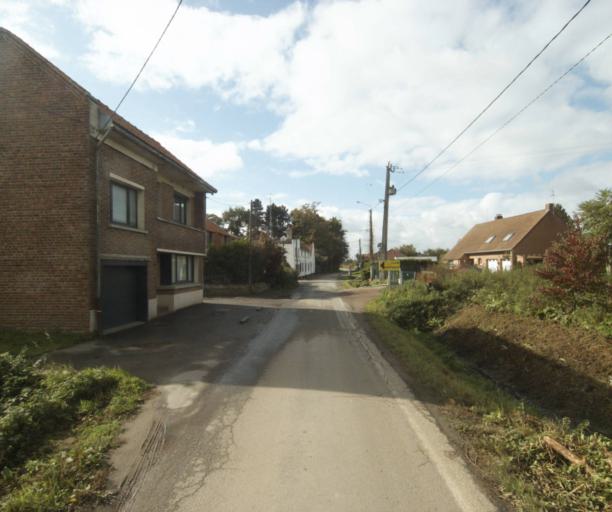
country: FR
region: Nord-Pas-de-Calais
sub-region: Departement du Nord
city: Verlinghem
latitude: 50.6820
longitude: 3.0177
